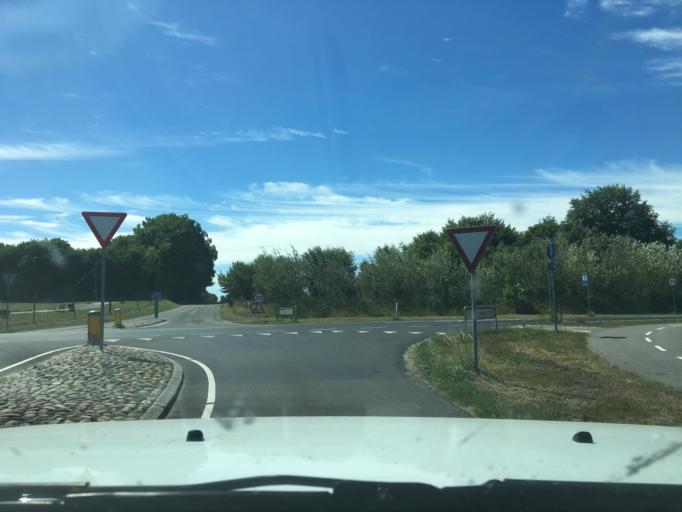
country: DK
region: Central Jutland
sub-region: Syddjurs Kommune
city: Ryomgard
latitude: 56.4301
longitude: 10.5673
